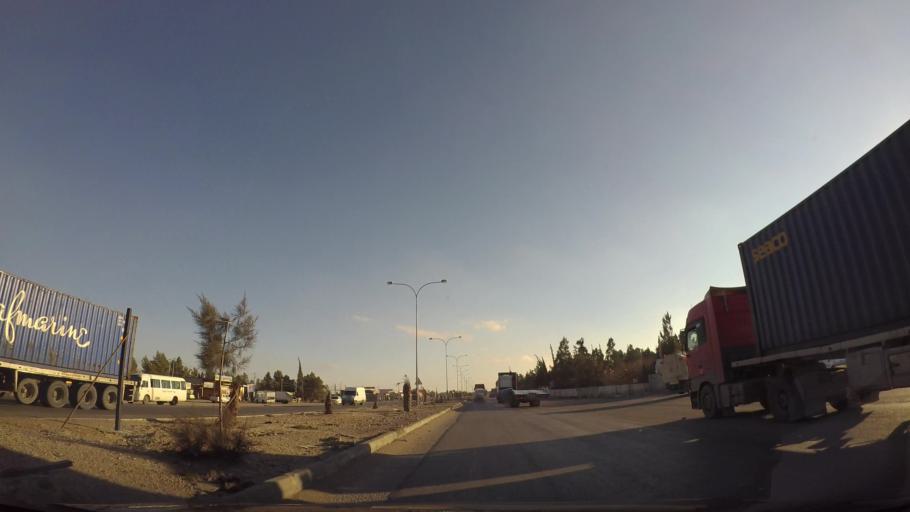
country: JO
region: Tafielah
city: Busayra
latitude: 30.5978
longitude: 35.8043
